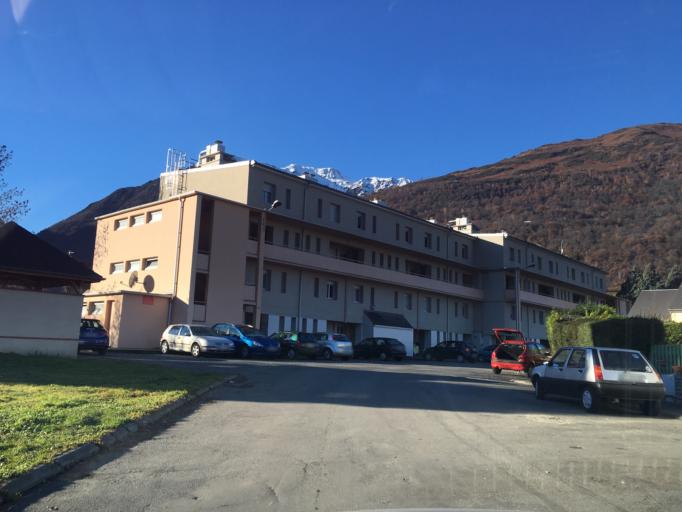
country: FR
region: Midi-Pyrenees
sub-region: Departement des Hautes-Pyrenees
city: Pierrefitte-Nestalas
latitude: 42.9628
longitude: -0.0693
